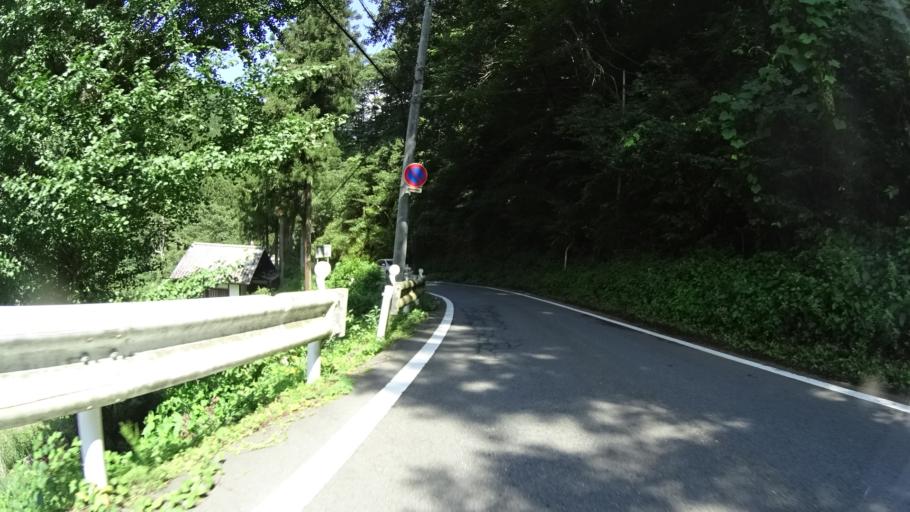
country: JP
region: Gunma
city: Tomioka
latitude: 36.0711
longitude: 138.8306
